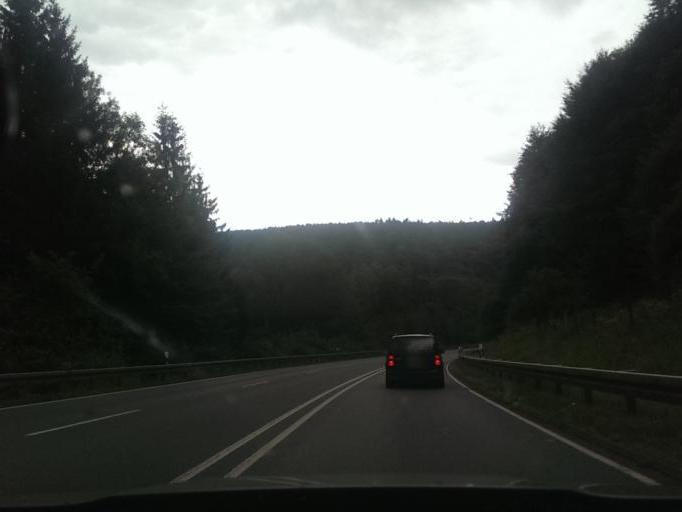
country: DE
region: North Rhine-Westphalia
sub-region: Regierungsbezirk Detmold
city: Horn
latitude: 51.8425
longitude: 8.9125
